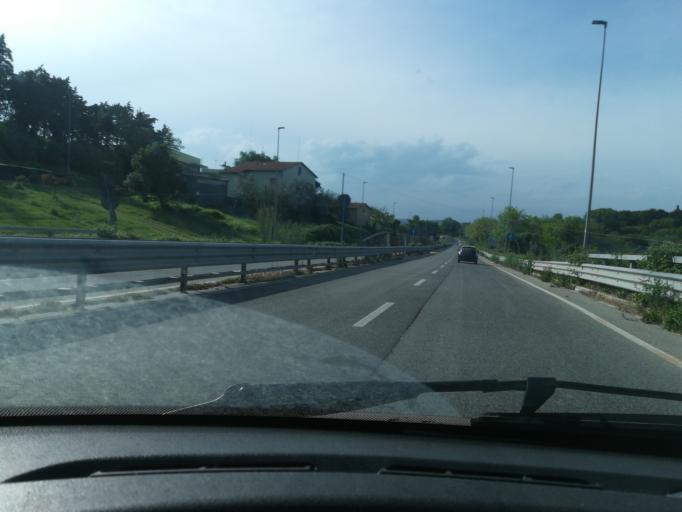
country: IT
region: The Marches
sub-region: Provincia di Macerata
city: Villa Potenza
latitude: 43.3124
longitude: 13.4389
